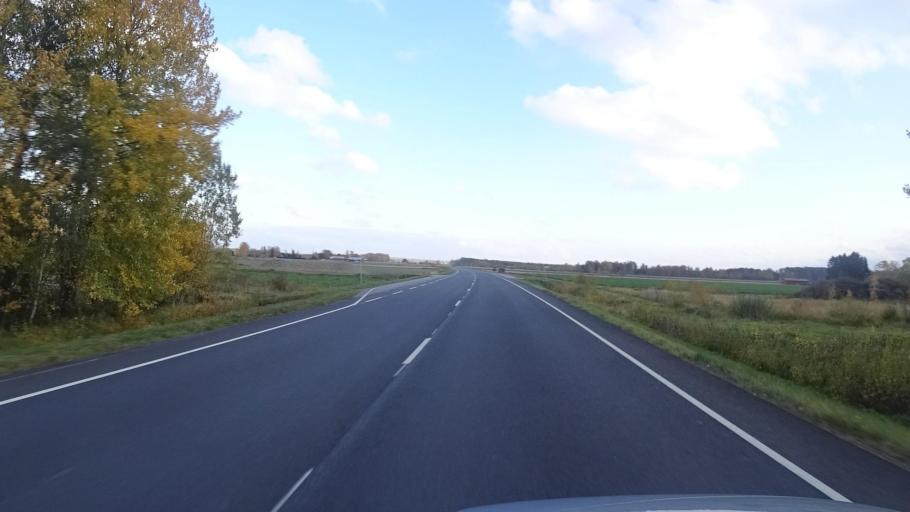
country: FI
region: Satakunta
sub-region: Rauma
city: Koeylioe
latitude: 61.0784
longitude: 22.2817
